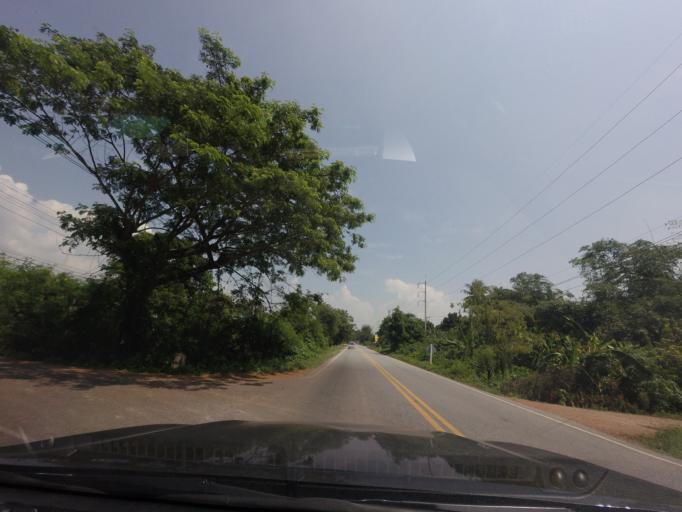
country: TH
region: Uttaradit
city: Thong Saen Khan
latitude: 17.4648
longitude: 100.2790
